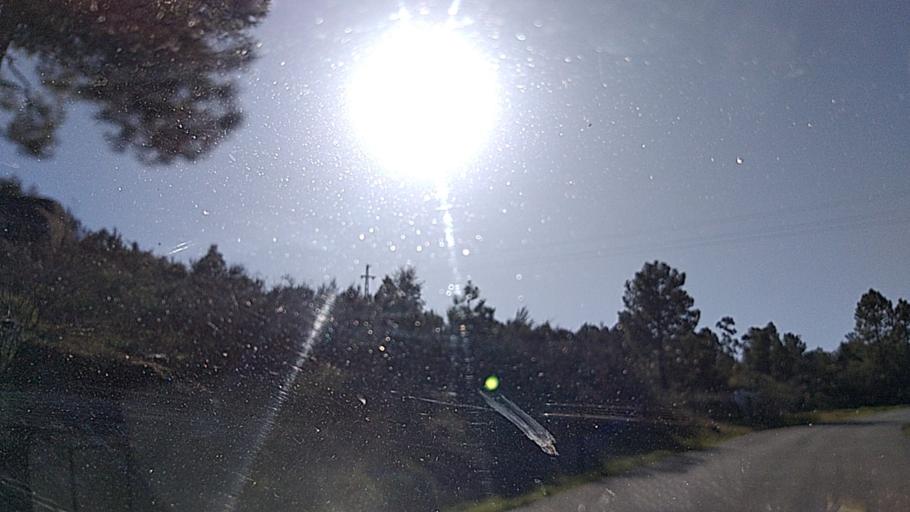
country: PT
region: Guarda
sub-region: Celorico da Beira
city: Celorico da Beira
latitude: 40.6823
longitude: -7.3973
